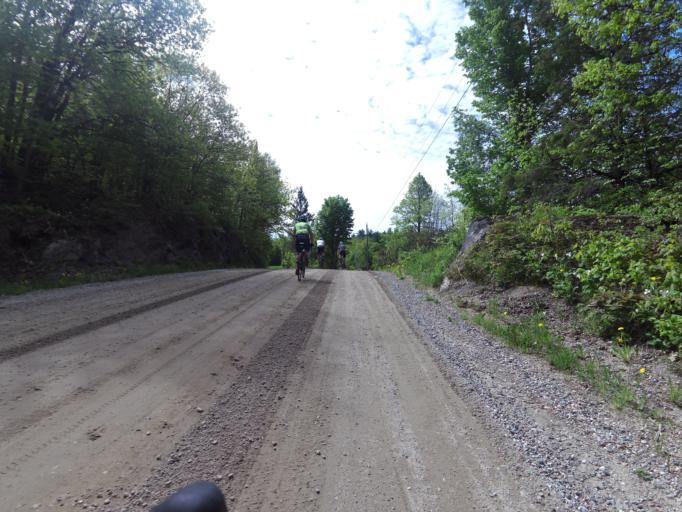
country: CA
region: Quebec
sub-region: Outaouais
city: Wakefield
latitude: 45.7996
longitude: -75.9818
